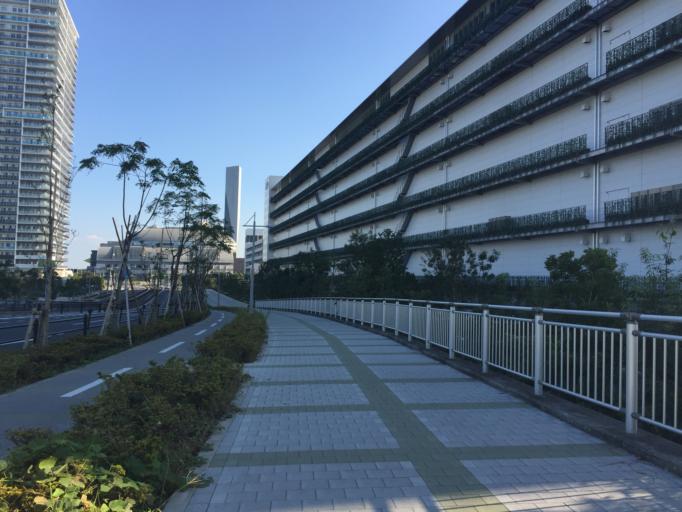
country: JP
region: Tokyo
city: Tokyo
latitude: 35.6377
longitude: 139.7802
